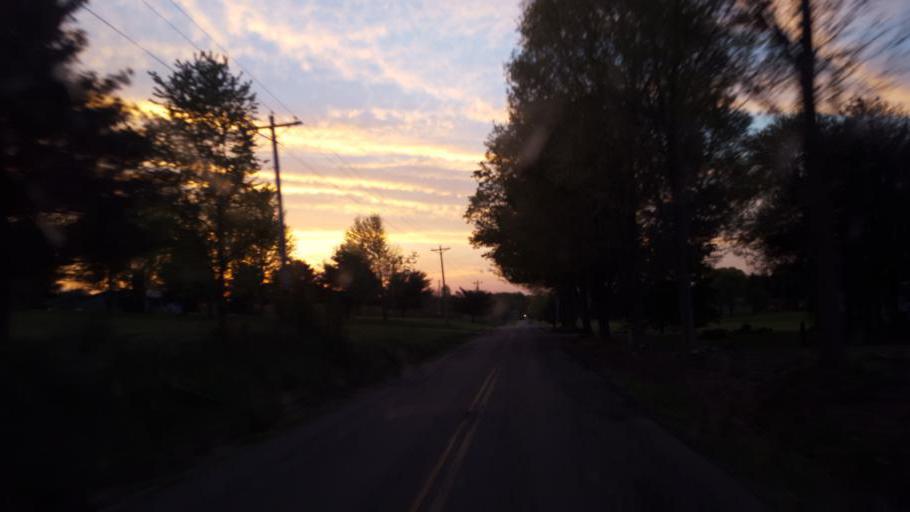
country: US
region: Ohio
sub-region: Knox County
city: Mount Vernon
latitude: 40.4724
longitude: -82.4310
